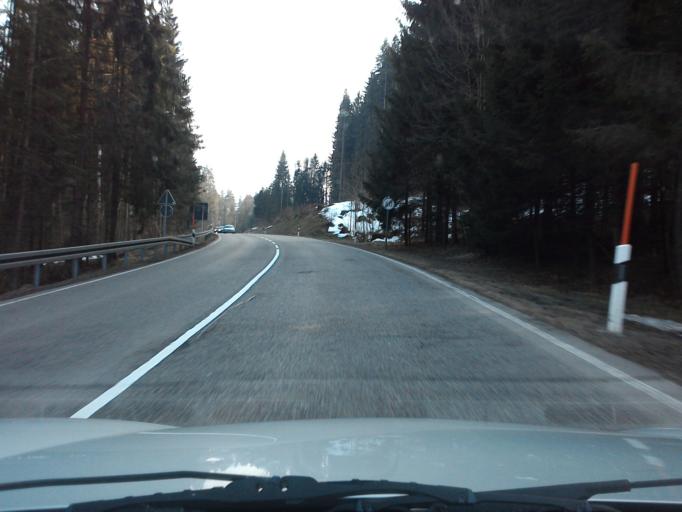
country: DE
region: Bavaria
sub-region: Swabia
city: Bolsterlang
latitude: 47.4816
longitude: 10.2660
